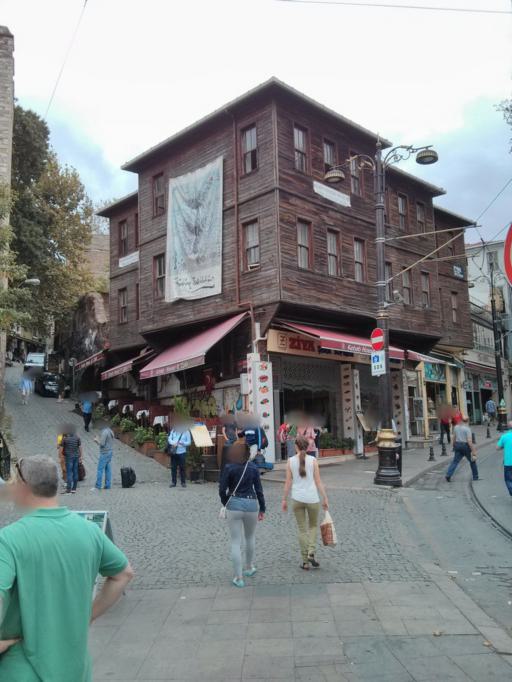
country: TR
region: Istanbul
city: Eminoenue
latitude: 41.0105
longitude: 28.9787
